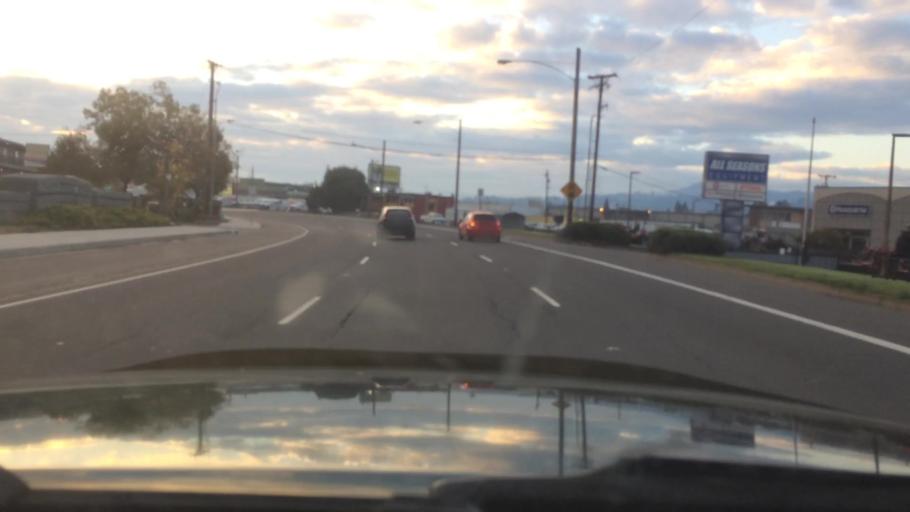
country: US
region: Oregon
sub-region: Lane County
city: Eugene
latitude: 44.0532
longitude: -123.1273
